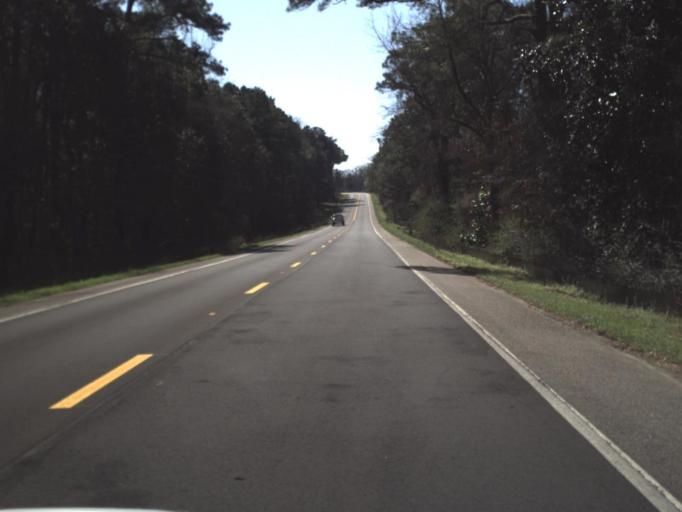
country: US
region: Florida
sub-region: Jackson County
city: Marianna
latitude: 30.6146
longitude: -85.1488
